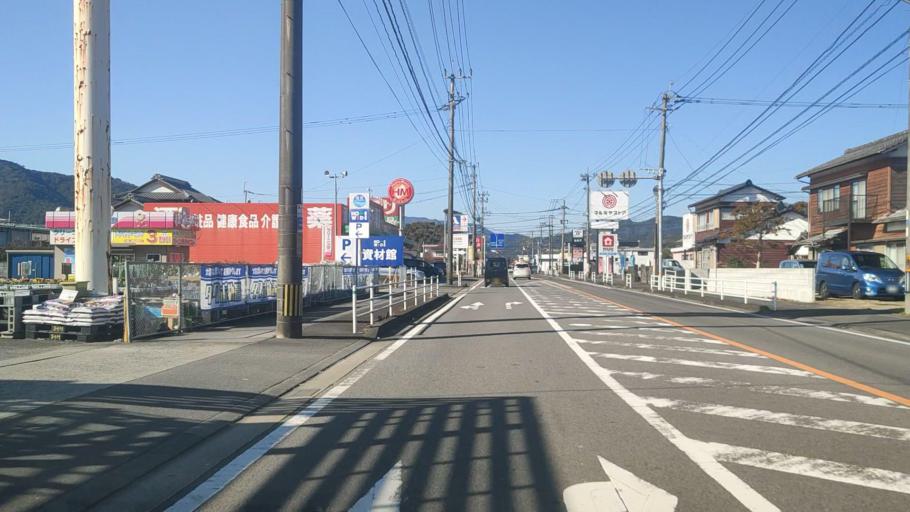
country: JP
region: Oita
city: Saiki
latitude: 32.9453
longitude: 131.9031
